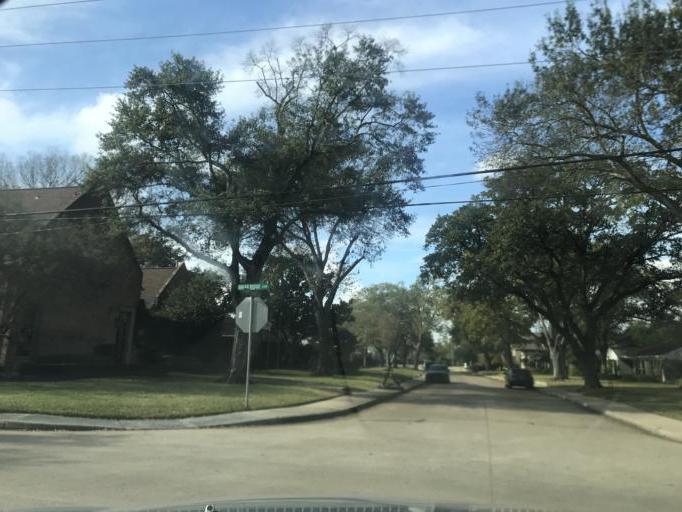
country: US
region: Texas
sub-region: Harris County
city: Hunters Creek Village
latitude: 29.7450
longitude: -95.4924
